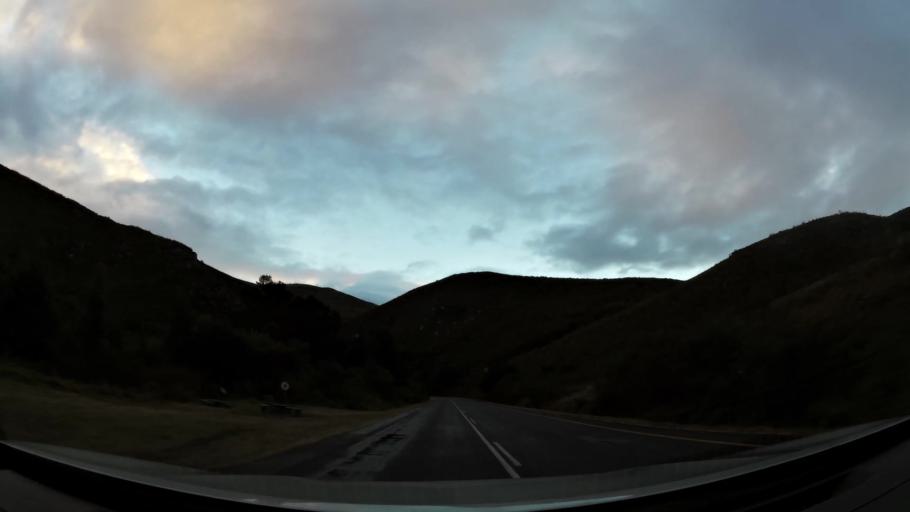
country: ZA
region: Western Cape
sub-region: Overberg District Municipality
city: Swellendam
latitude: -33.9870
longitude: 20.7186
